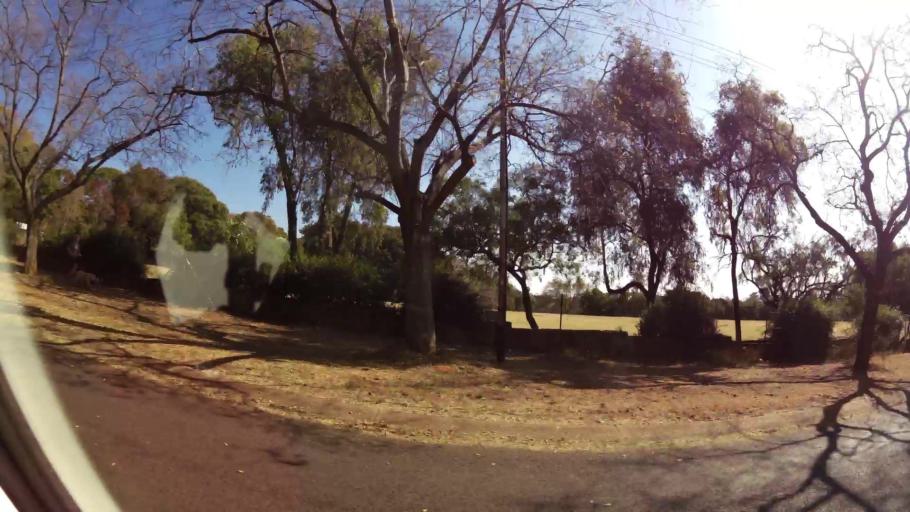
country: ZA
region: Gauteng
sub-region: City of Tshwane Metropolitan Municipality
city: Pretoria
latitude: -25.7634
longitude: 28.2422
